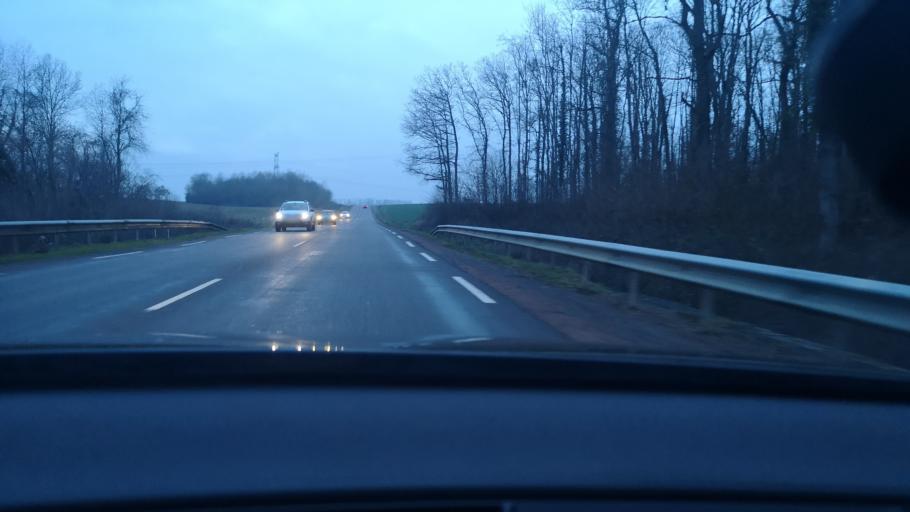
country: FR
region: Bourgogne
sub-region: Departement de Saone-et-Loire
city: Verdun-sur-le-Doubs
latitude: 47.0052
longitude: 5.0138
